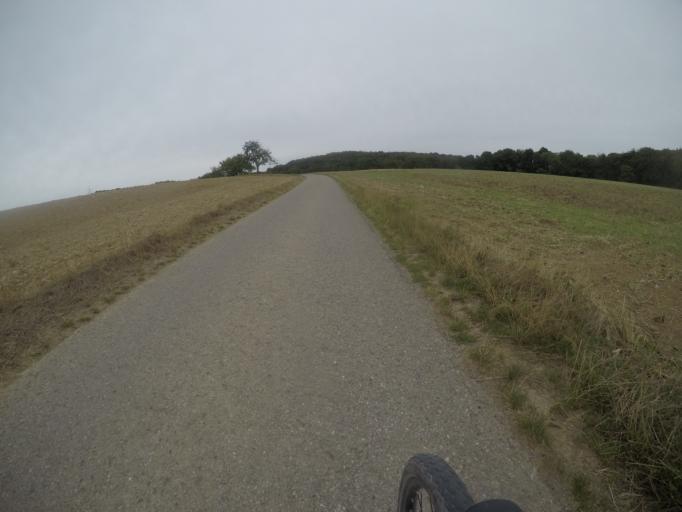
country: DE
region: Baden-Wuerttemberg
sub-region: Karlsruhe Region
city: Wurmberg
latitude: 48.8662
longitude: 8.8318
